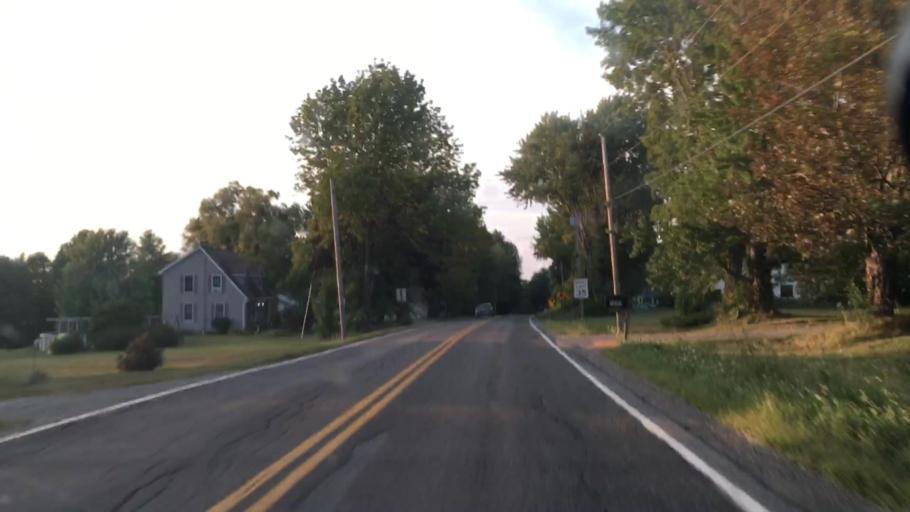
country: US
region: Maine
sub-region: Penobscot County
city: Hermon
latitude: 44.7297
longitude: -68.9615
